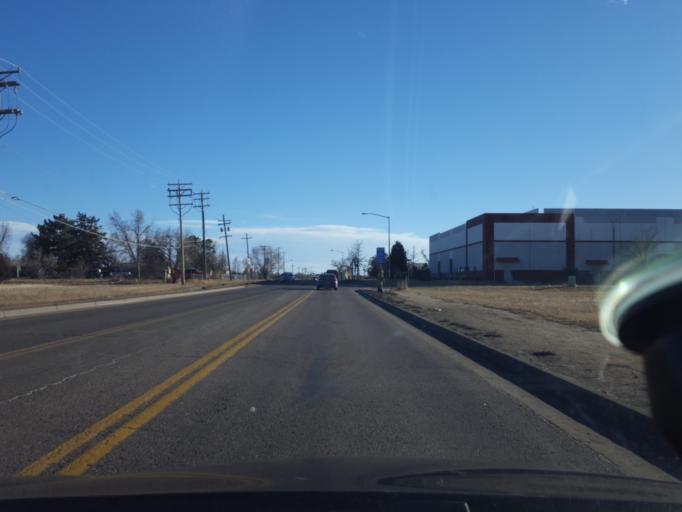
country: US
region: Colorado
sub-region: Adams County
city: Aurora
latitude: 39.7499
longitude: -104.7724
